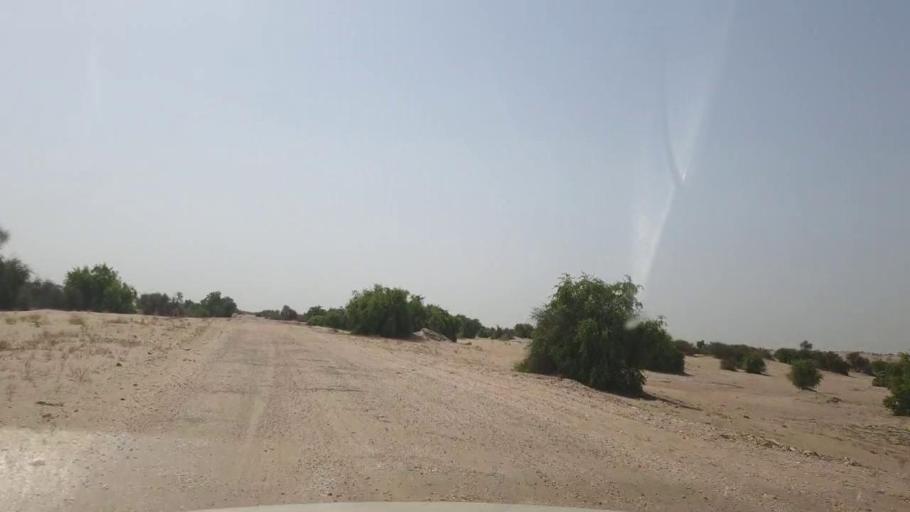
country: PK
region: Sindh
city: Rohri
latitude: 27.4510
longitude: 69.2289
